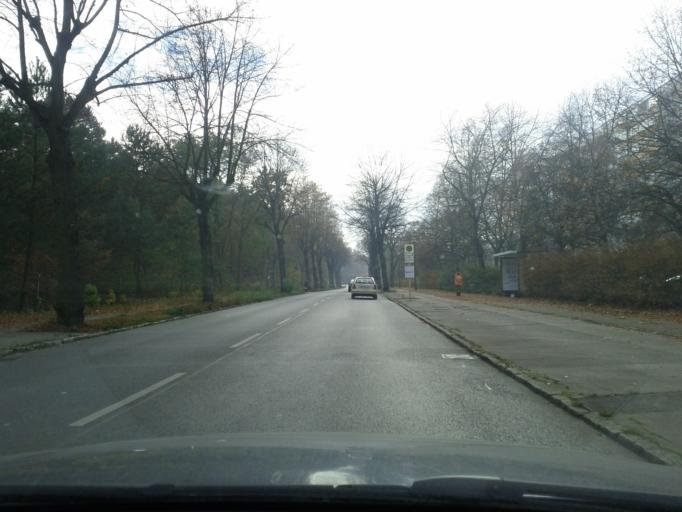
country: DE
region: Berlin
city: Berlin Koepenick
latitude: 52.4441
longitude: 13.5935
